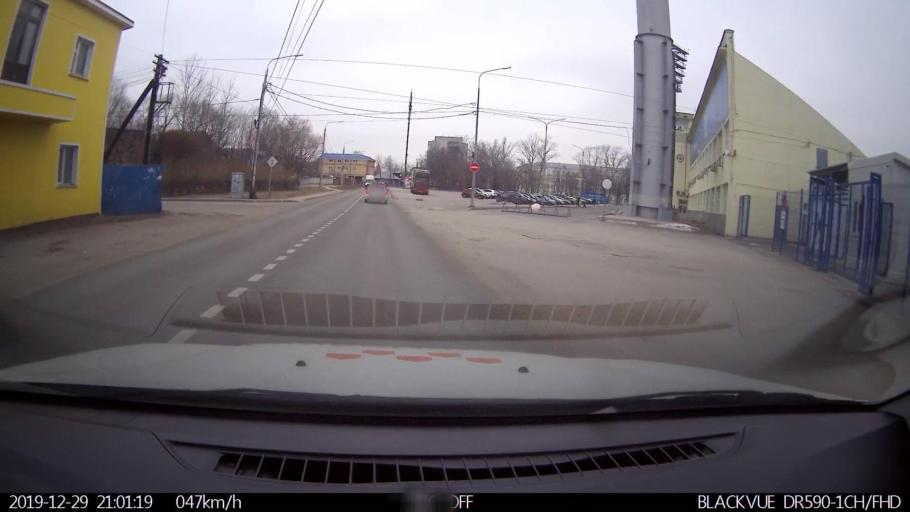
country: RU
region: Nizjnij Novgorod
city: Nizhniy Novgorod
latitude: 56.3085
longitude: 43.9279
